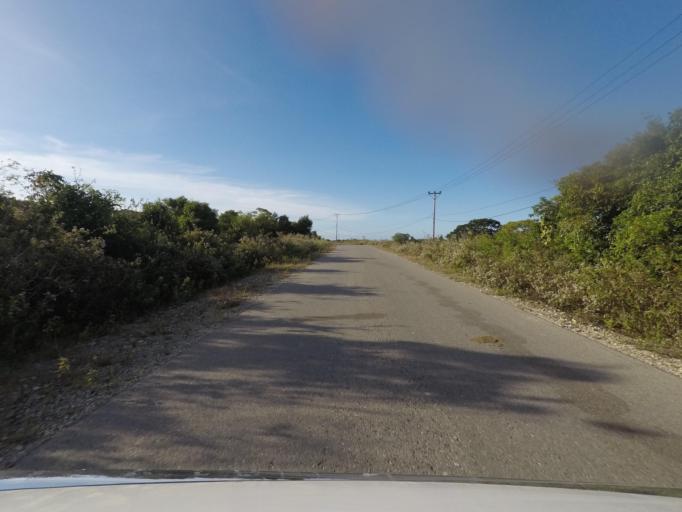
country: TL
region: Lautem
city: Lospalos
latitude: -8.3914
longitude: 127.0102
